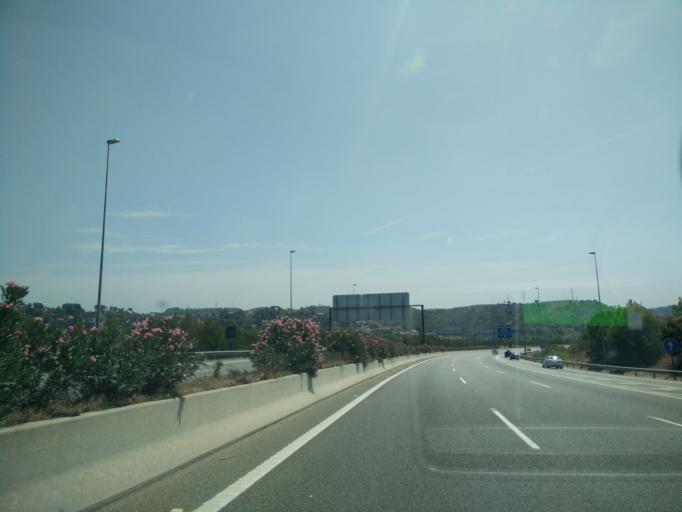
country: ES
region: Catalonia
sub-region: Provincia de Barcelona
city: Abrera
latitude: 41.4989
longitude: 1.9150
